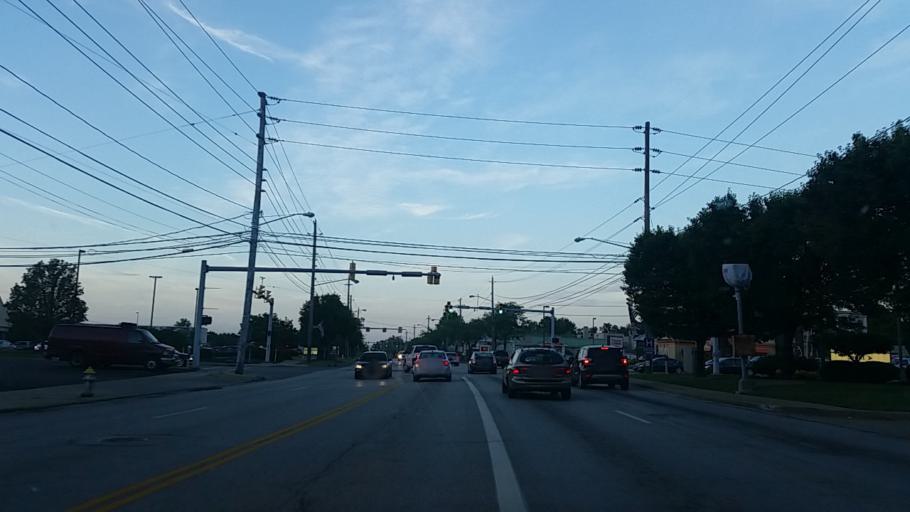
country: US
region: Ohio
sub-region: Cuyahoga County
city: Parma Heights
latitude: 41.3883
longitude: -81.7645
